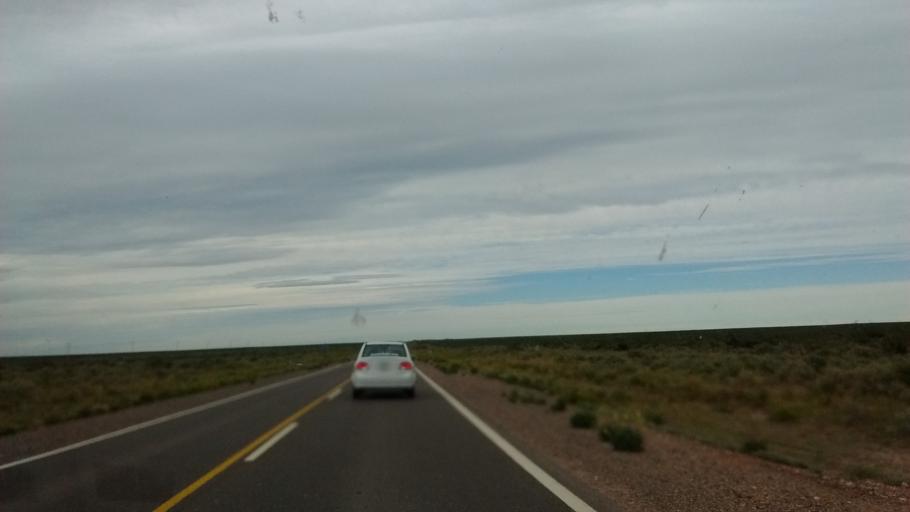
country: AR
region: Rio Negro
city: Contraalmirante Cordero
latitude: -38.3283
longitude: -68.0079
